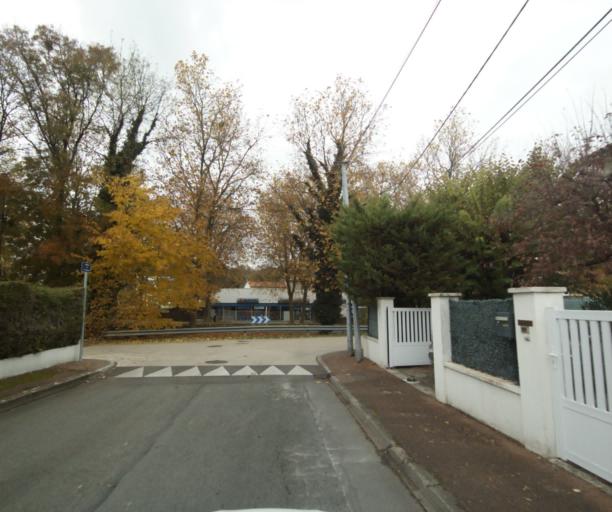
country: FR
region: Poitou-Charentes
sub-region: Departement de la Charente-Maritime
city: Saintes
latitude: 45.7409
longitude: -0.6495
